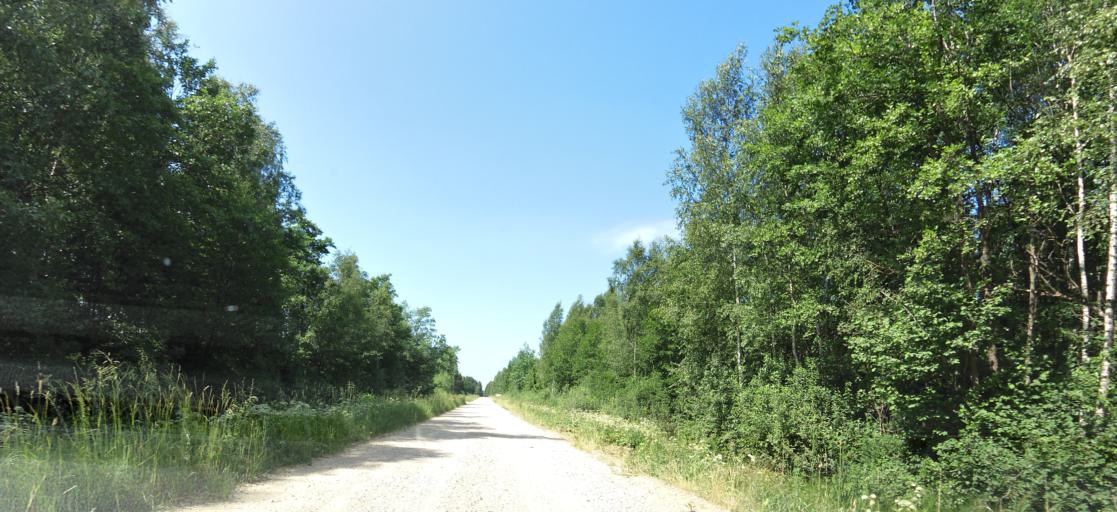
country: LT
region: Panevezys
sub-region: Birzai
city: Birzai
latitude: 56.2179
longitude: 24.9326
